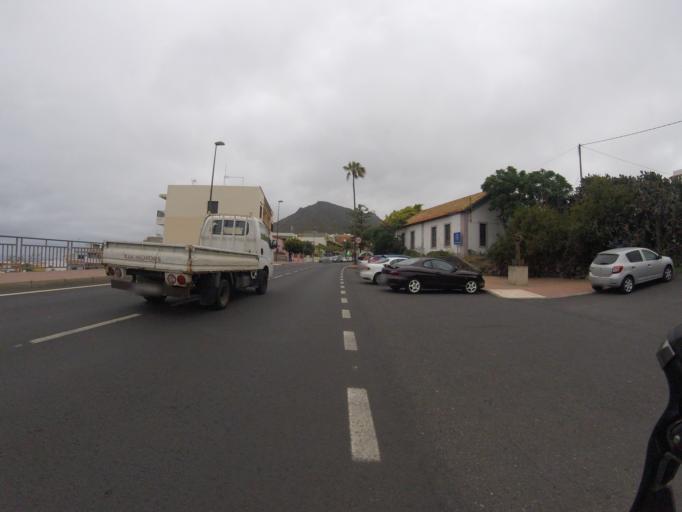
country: ES
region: Canary Islands
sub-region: Provincia de Santa Cruz de Tenerife
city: Tegueste
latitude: 28.5336
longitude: -16.3670
